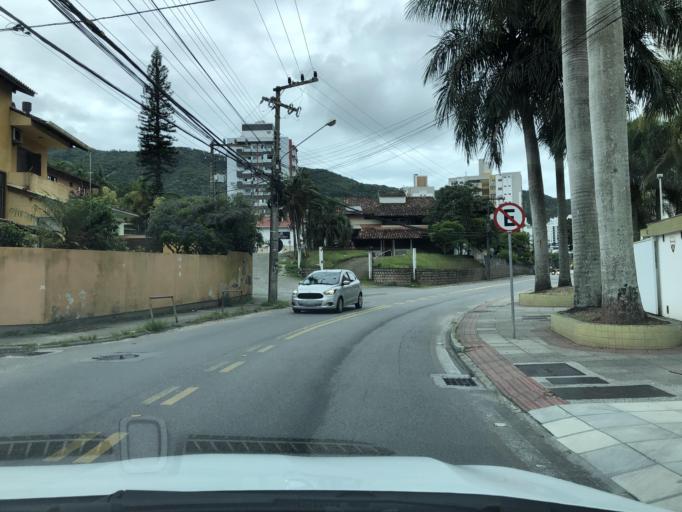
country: BR
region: Santa Catarina
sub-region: Florianopolis
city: Itacorubi
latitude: -27.5823
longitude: -48.5022
